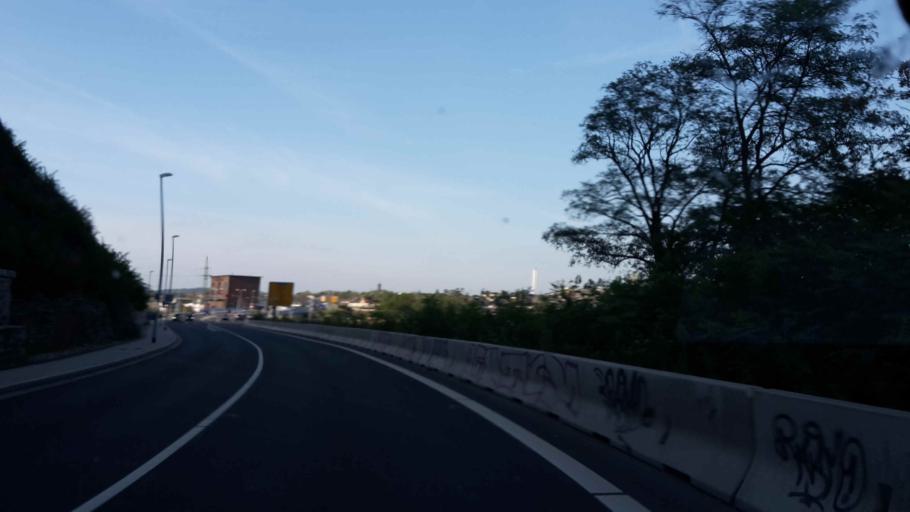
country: DE
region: North Rhine-Westphalia
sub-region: Regierungsbezirk Arnsberg
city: Hagen
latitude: 51.3623
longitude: 7.4574
